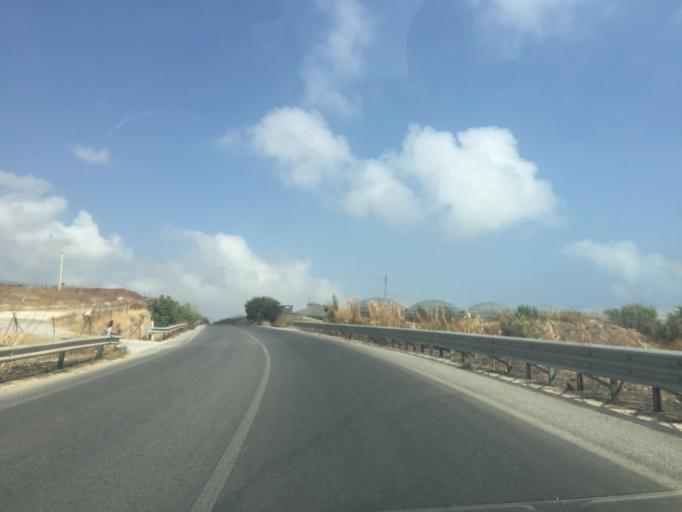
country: IT
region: Sicily
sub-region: Ragusa
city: Donnalucata
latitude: 36.7734
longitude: 14.6198
